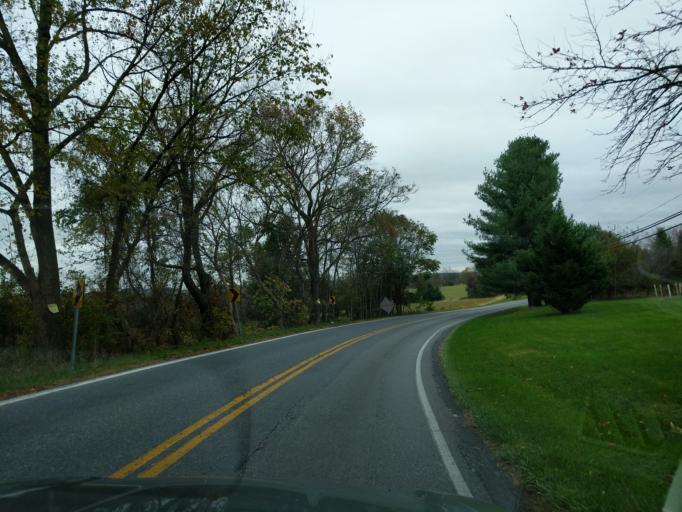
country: US
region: Maryland
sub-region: Frederick County
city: Spring Ridge
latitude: 39.4091
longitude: -77.2949
